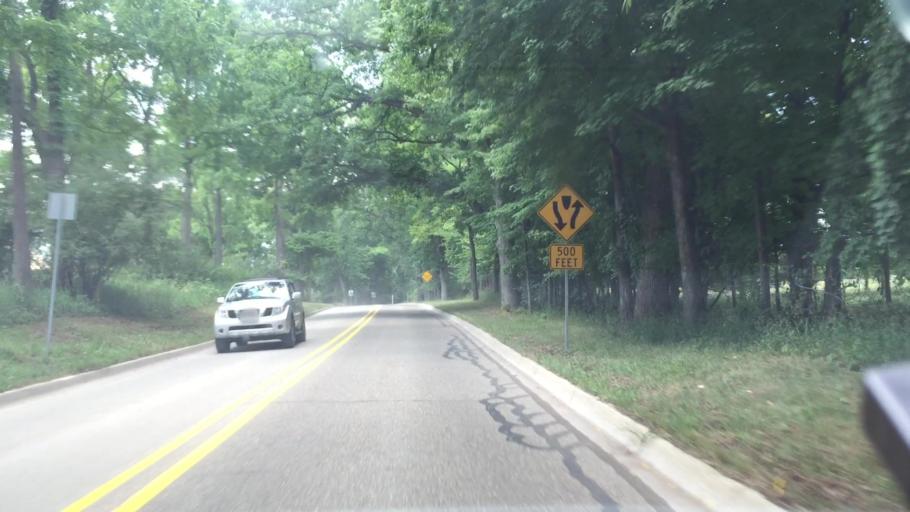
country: US
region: Michigan
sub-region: Oakland County
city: Auburn Hills
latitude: 42.6566
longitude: -83.2092
